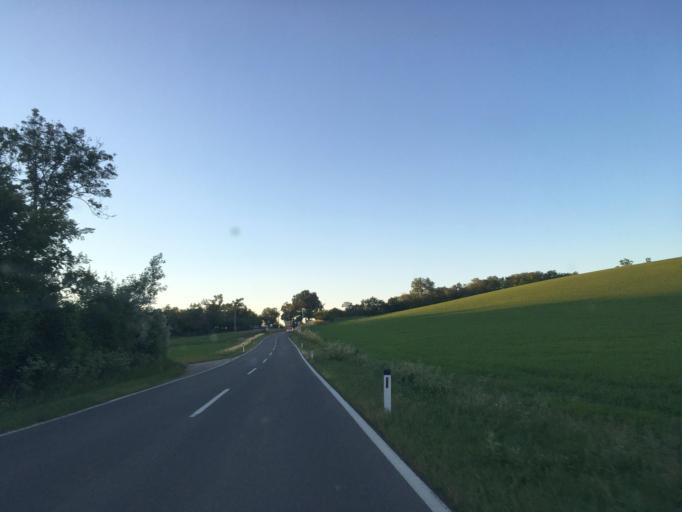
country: AT
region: Lower Austria
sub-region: Politischer Bezirk Modling
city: Gumpoldskirchen
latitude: 48.0629
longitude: 16.2876
